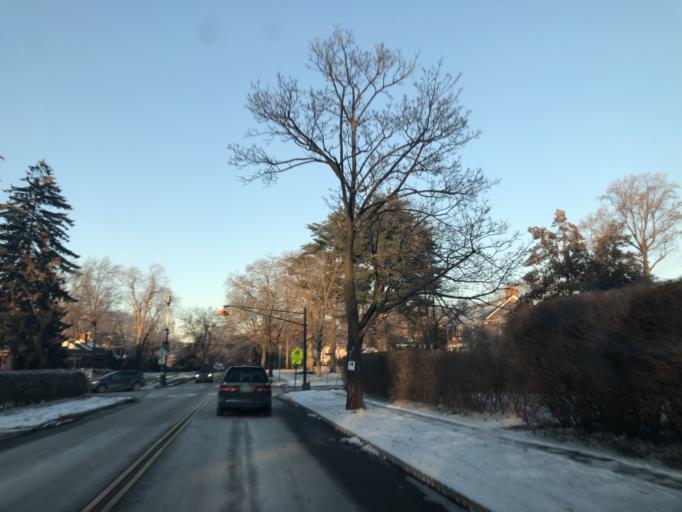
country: US
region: New Jersey
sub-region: Essex County
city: Irvington
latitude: 40.7480
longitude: -74.2412
